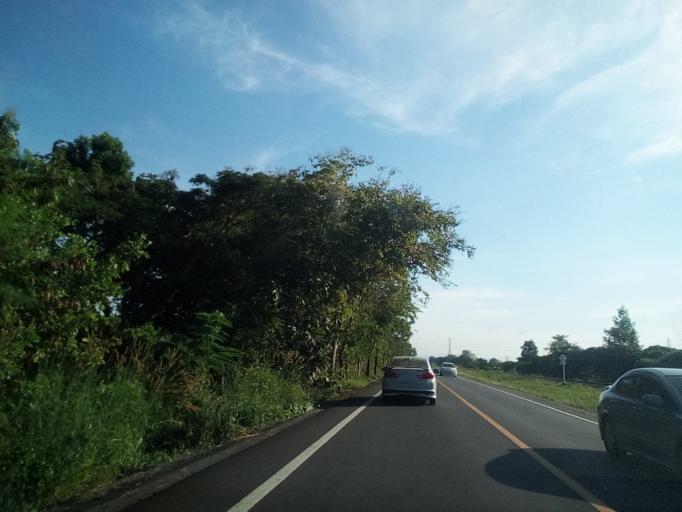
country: TH
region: Chiang Mai
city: Saraphi
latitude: 18.6703
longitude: 99.0447
